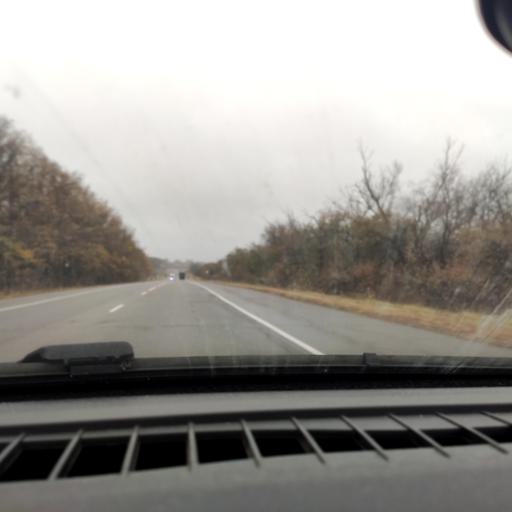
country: RU
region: Voronezj
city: Kolodeznyy
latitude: 51.3295
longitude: 39.0264
